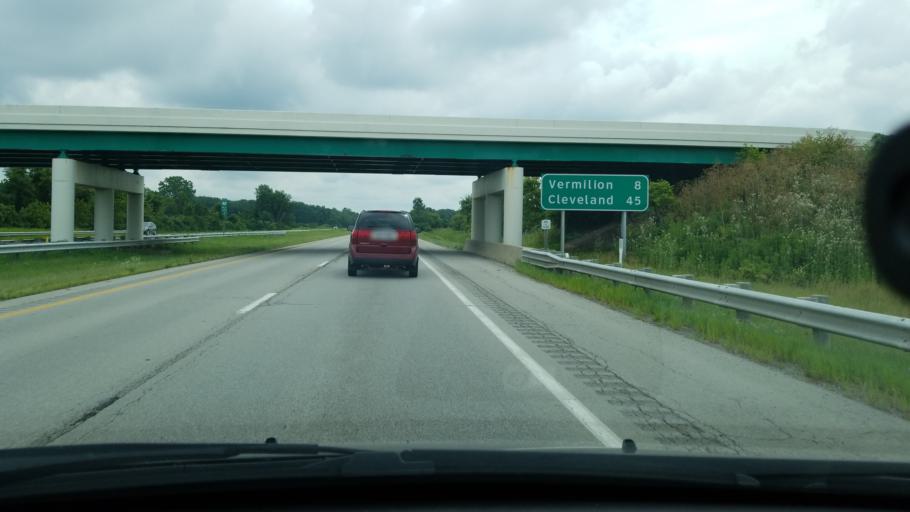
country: US
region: Ohio
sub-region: Erie County
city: Huron
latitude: 41.3678
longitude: -82.4723
